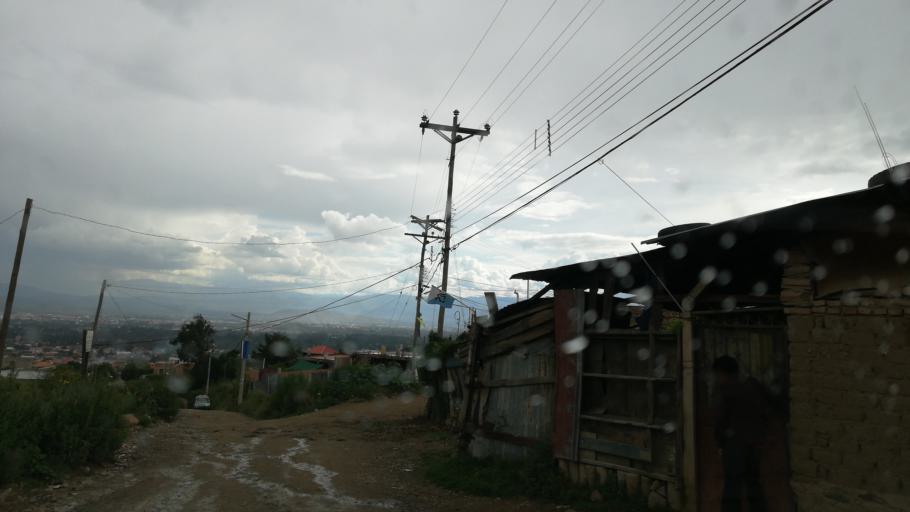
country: BO
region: Cochabamba
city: Cochabamba
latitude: -17.3298
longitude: -66.1932
